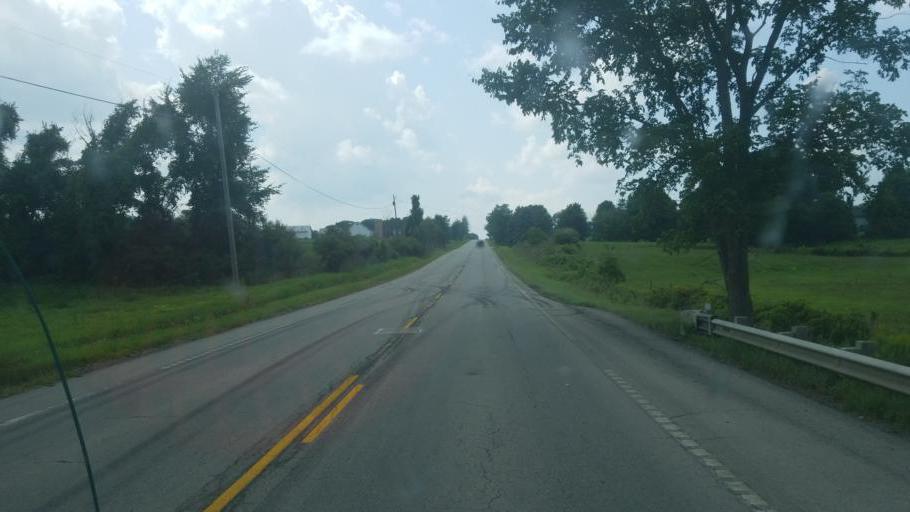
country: US
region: Ohio
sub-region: Huron County
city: New London
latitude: 41.0292
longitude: -82.4216
